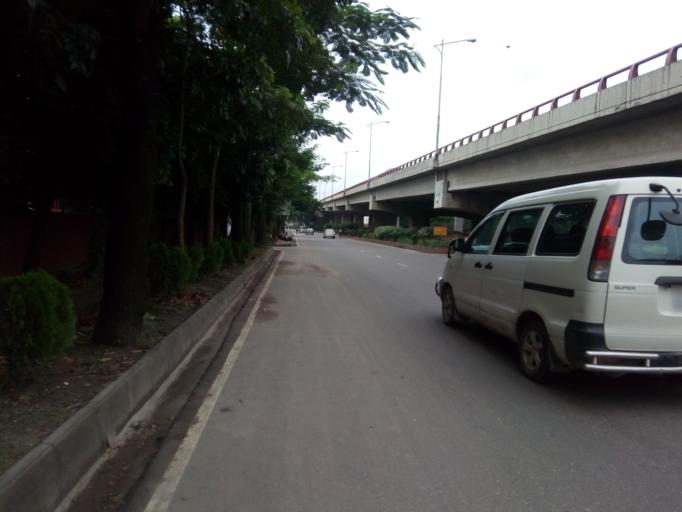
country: BD
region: Dhaka
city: Paltan
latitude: 23.8131
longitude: 90.4043
